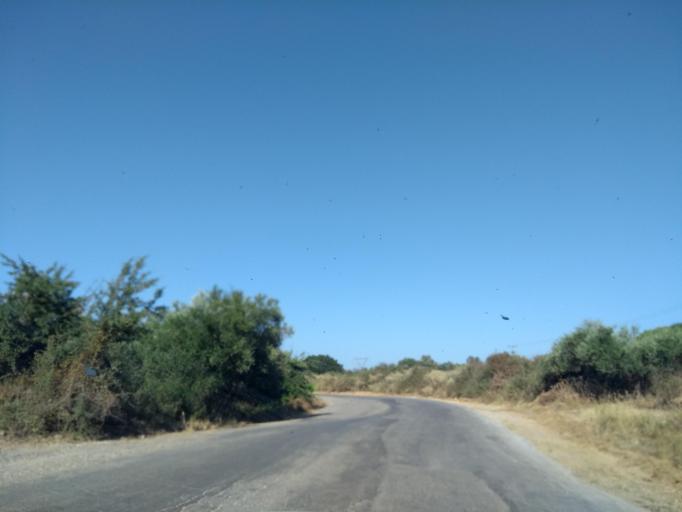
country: GR
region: Crete
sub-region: Nomos Chanias
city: Georgioupolis
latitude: 35.3677
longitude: 24.2285
